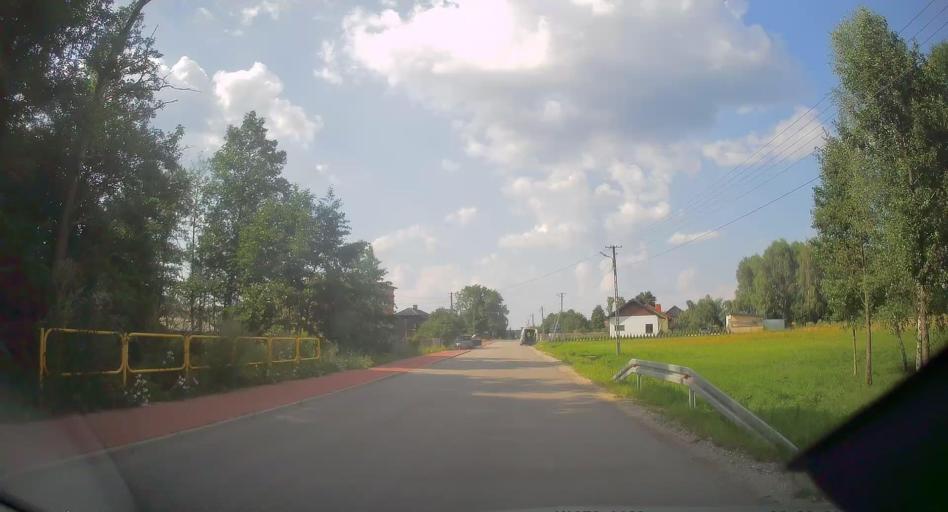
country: PL
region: Swietokrzyskie
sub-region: Powiat konecki
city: Radoszyce
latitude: 51.1117
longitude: 20.2630
